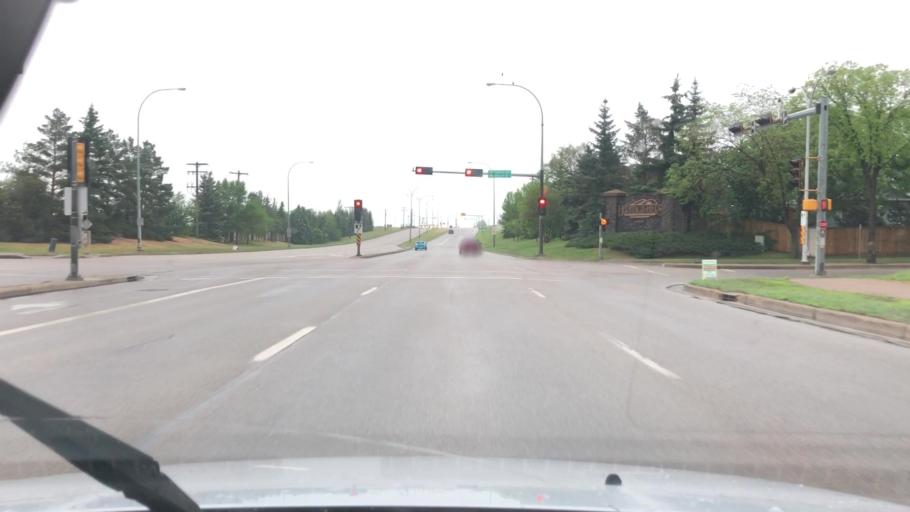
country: CA
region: Alberta
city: Sherwood Park
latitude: 53.5411
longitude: -113.2556
